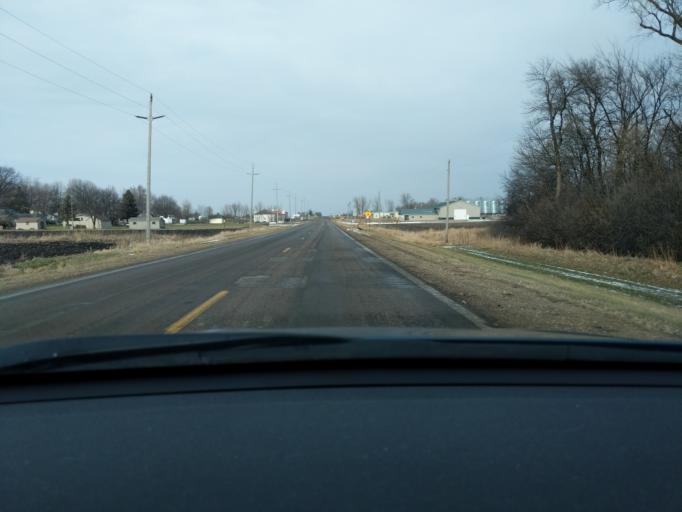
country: US
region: Minnesota
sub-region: Renville County
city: Renville
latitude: 44.7840
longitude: -95.3409
